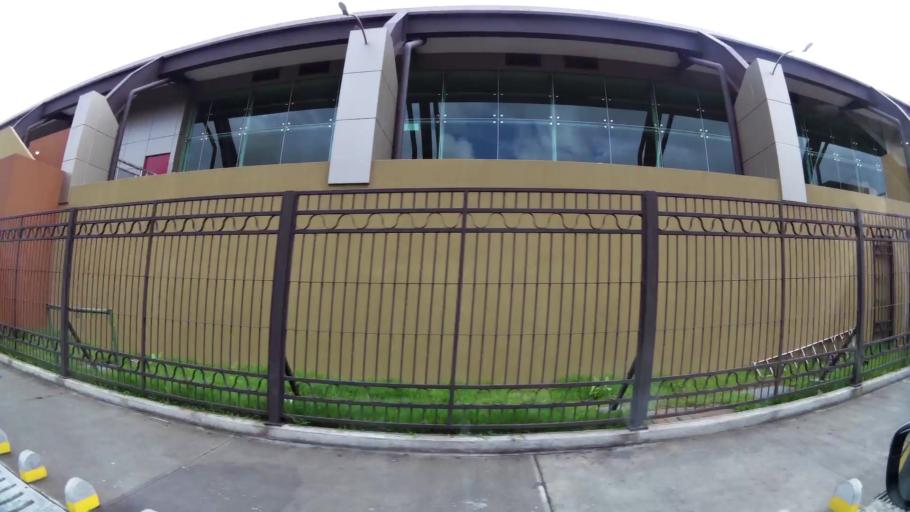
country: CR
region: San Jose
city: San Jose
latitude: 9.9360
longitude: -84.0700
